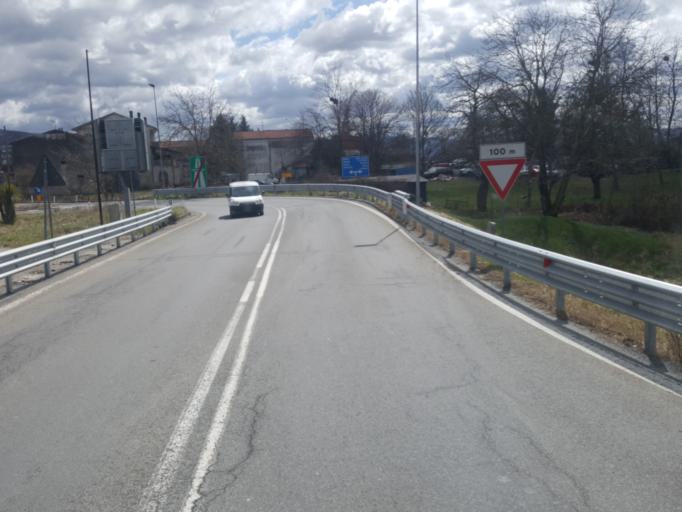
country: IT
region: Calabria
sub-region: Provincia di Cosenza
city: Santo Stefano di Rogliano
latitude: 39.1998
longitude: 16.3133
